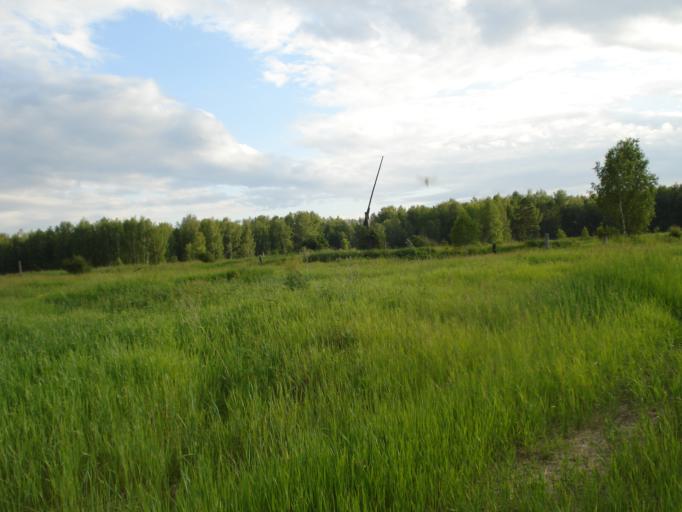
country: RU
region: Krasnoyarskiy
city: Predivinsk
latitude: 56.9734
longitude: 92.8761
